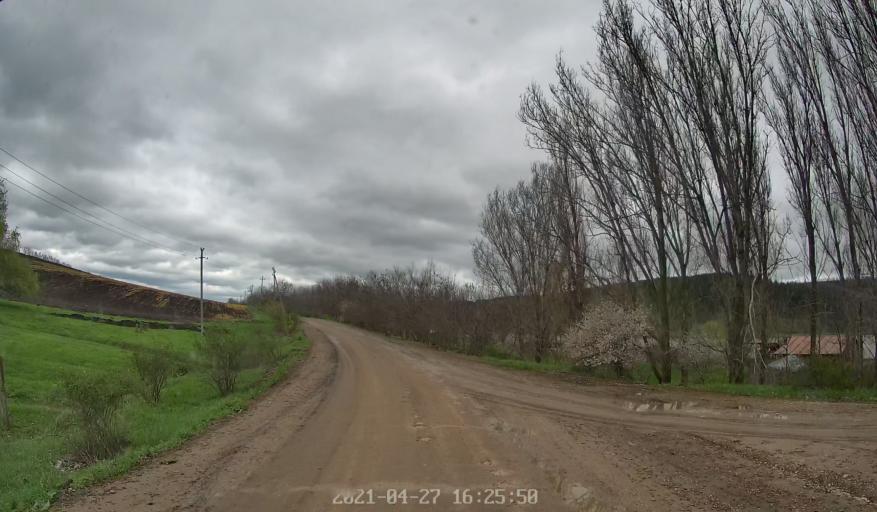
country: MD
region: Chisinau
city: Singera
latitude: 46.9827
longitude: 29.0216
